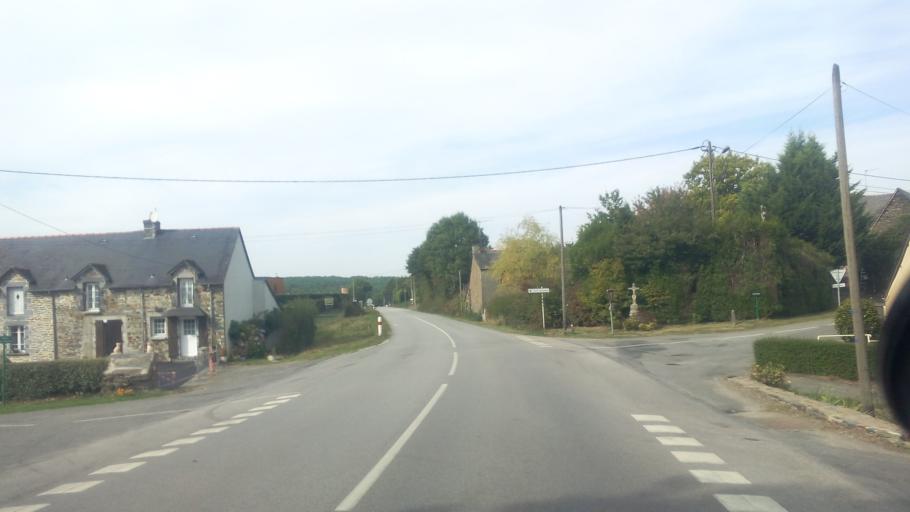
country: FR
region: Brittany
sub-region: Departement du Morbihan
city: La Gacilly
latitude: 47.7502
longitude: -2.1271
